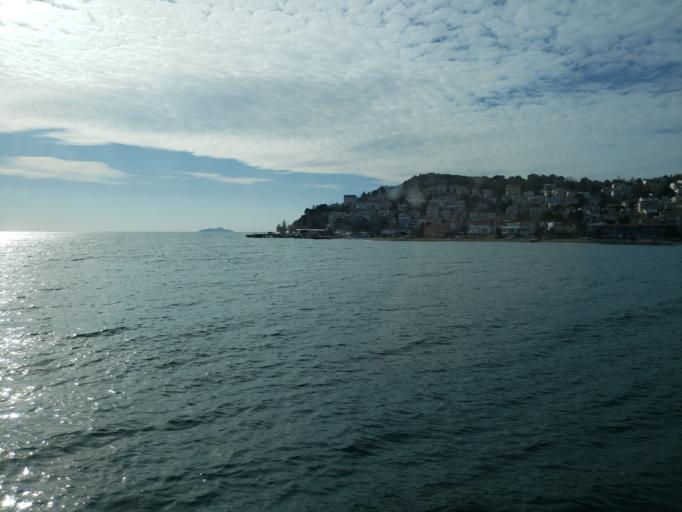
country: TR
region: Istanbul
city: Kinali
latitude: 40.9065
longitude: 29.0600
